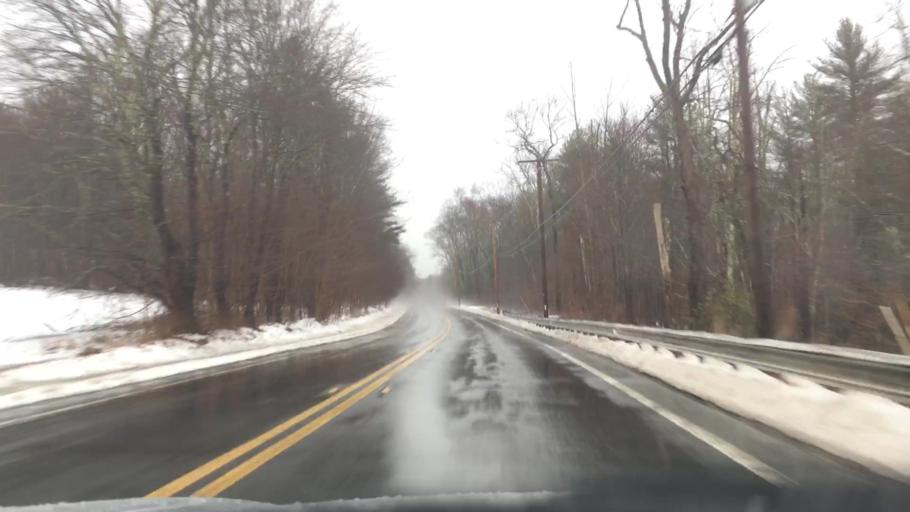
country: US
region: Massachusetts
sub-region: Hampshire County
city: Belchertown
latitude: 42.3145
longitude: -72.4061
